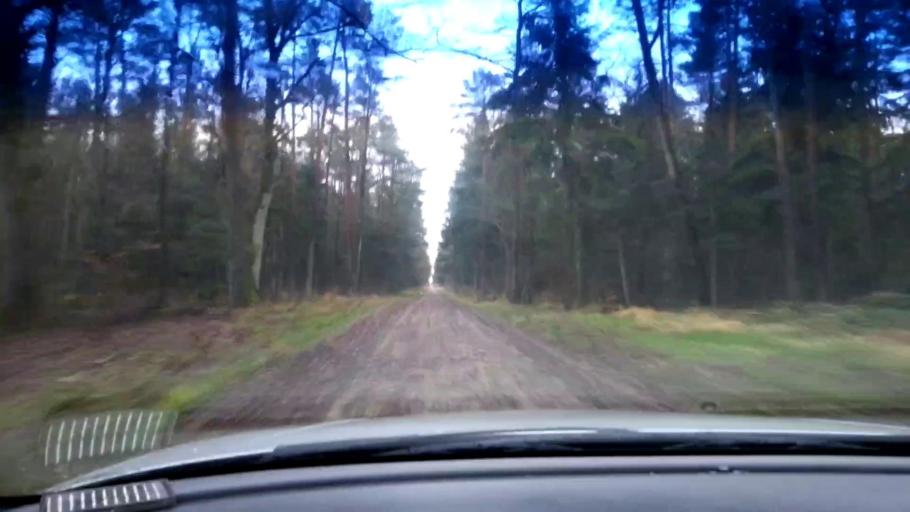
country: DE
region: Bavaria
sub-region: Upper Franconia
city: Breitengussbach
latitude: 49.9578
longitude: 10.9005
